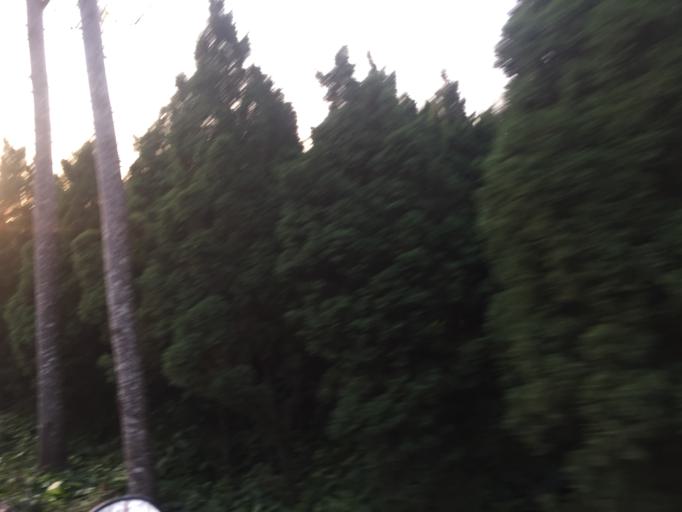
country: VN
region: Ha Noi
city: Chuc Son
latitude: 20.9063
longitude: 105.7282
